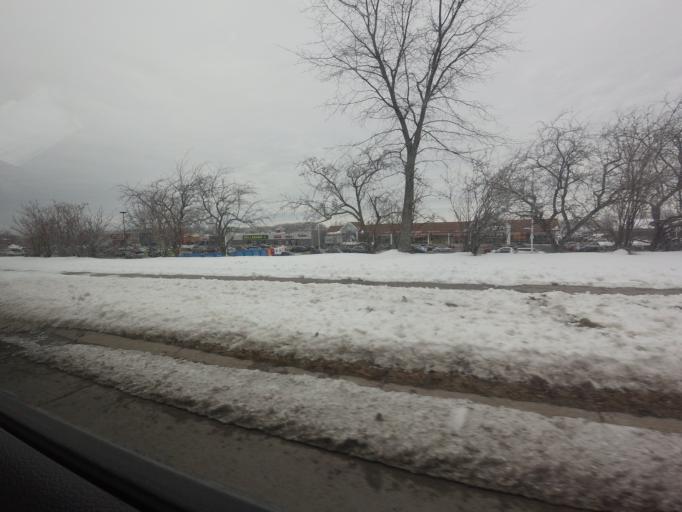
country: CA
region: New Brunswick
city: Oromocto
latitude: 45.8513
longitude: -66.4729
